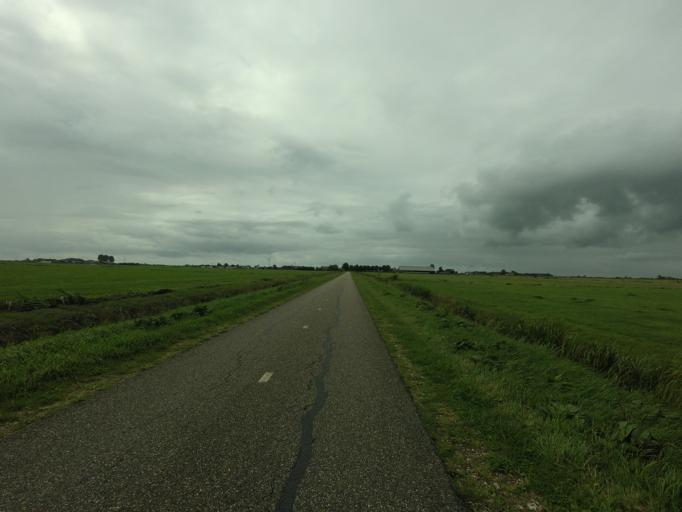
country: NL
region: Friesland
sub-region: Sudwest Fryslan
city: Workum
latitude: 52.9756
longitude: 5.5050
